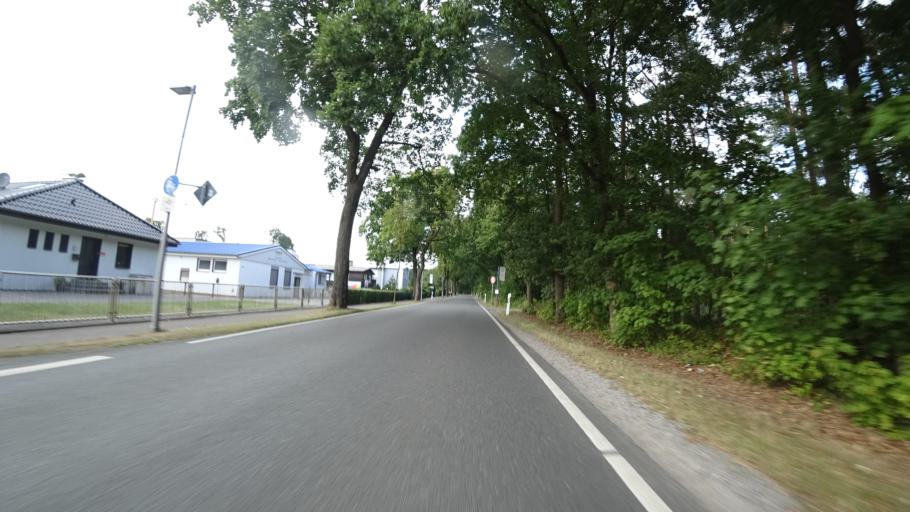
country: DE
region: North Rhine-Westphalia
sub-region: Regierungsbezirk Detmold
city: Steinhagen
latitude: 51.9844
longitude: 8.4630
